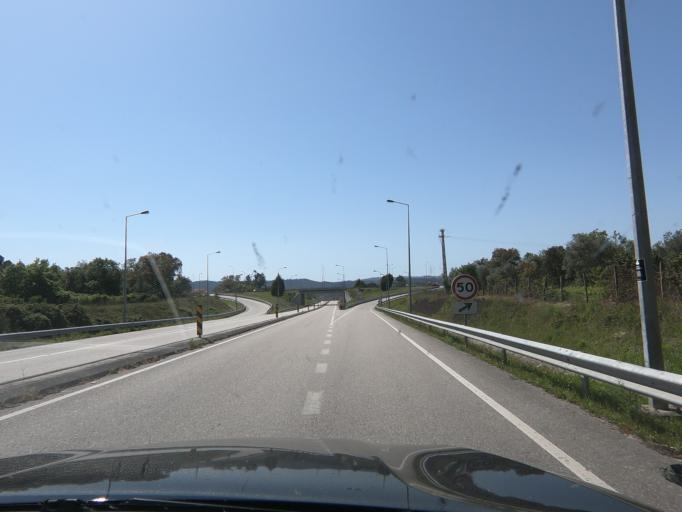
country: PT
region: Coimbra
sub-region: Lousa
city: Lousa
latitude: 40.1282
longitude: -8.2460
